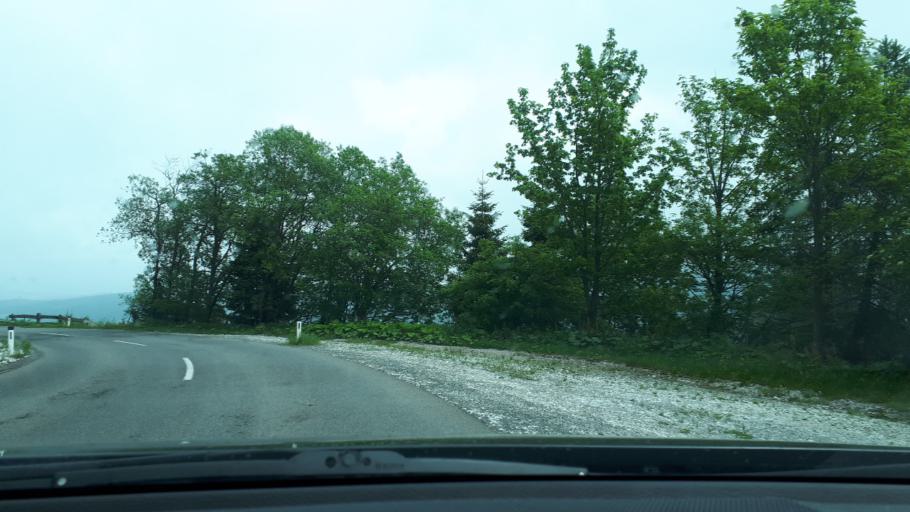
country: AT
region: Styria
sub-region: Politischer Bezirk Voitsberg
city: Modriach
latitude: 46.9240
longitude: 15.0168
